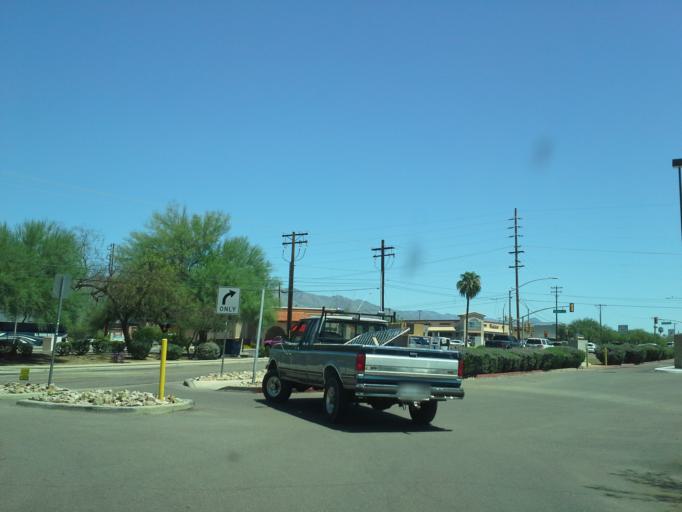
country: US
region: Arizona
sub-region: Pima County
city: Flowing Wells
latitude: 32.2827
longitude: -110.9796
